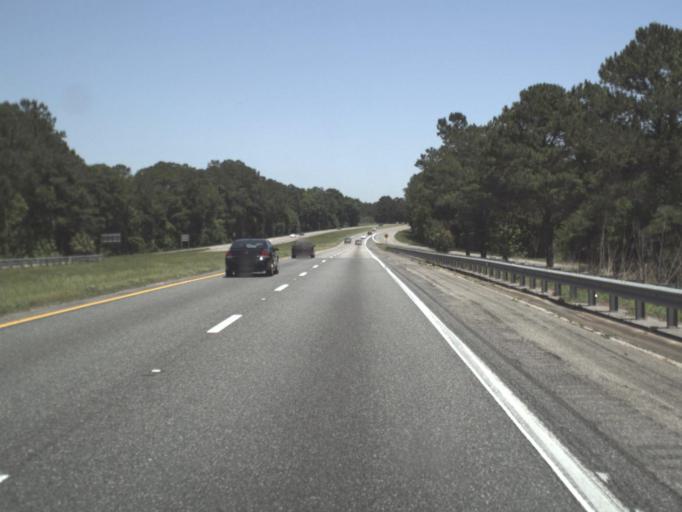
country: US
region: Florida
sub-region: Jefferson County
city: Monticello
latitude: 30.4879
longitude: -84.0240
